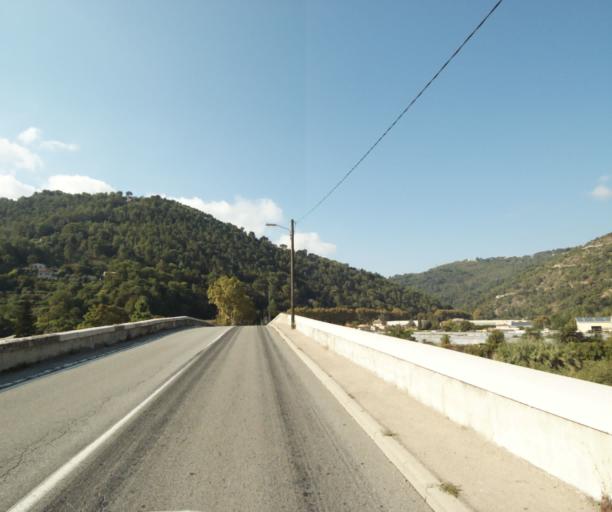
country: FR
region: Provence-Alpes-Cote d'Azur
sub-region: Departement des Alpes-Maritimes
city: Cantaron
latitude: 43.7673
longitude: 7.3307
